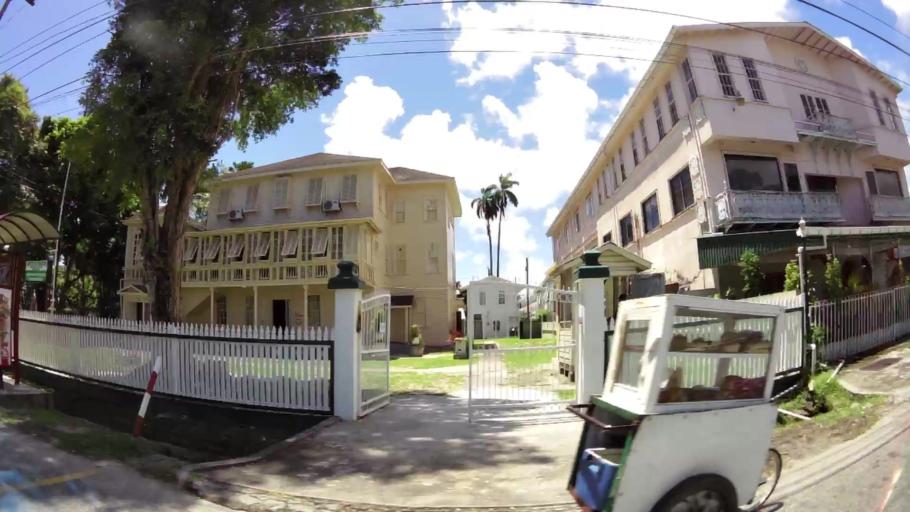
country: GY
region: Demerara-Mahaica
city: Georgetown
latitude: 6.8173
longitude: -58.1640
